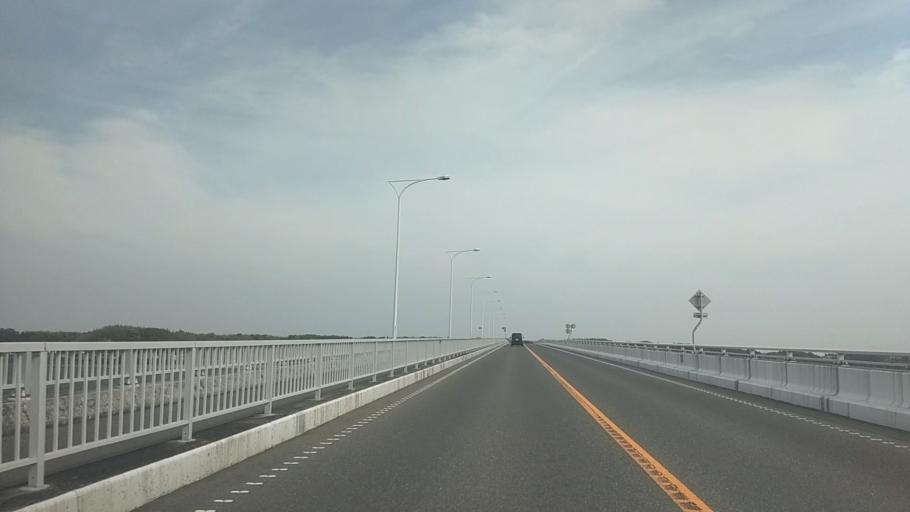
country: JP
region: Shizuoka
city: Kosai-shi
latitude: 34.7328
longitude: 137.6224
